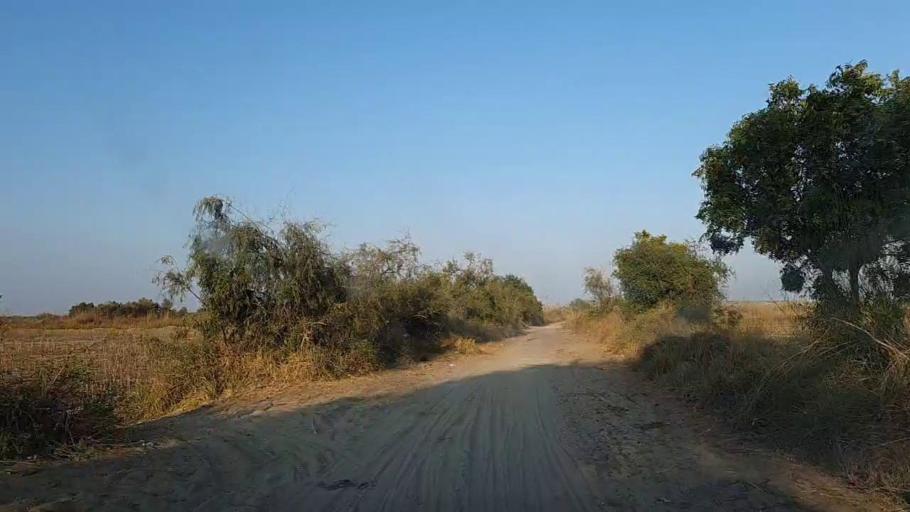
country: PK
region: Sindh
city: Sanghar
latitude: 26.2952
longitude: 68.9847
